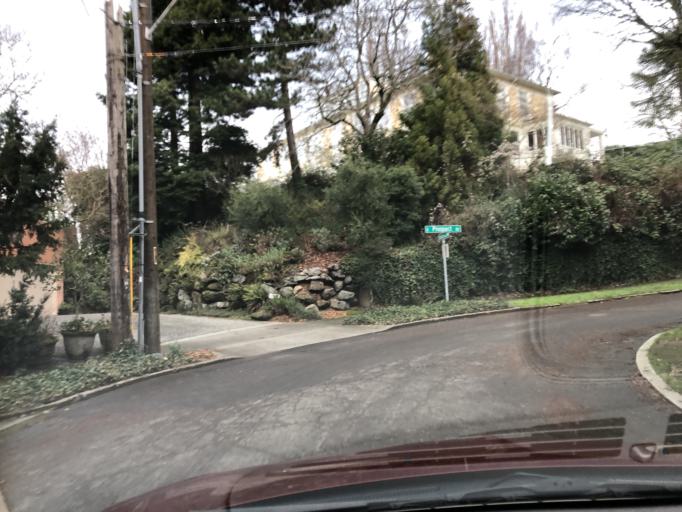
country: US
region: Washington
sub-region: King County
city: Seattle
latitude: 47.6291
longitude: -122.3247
